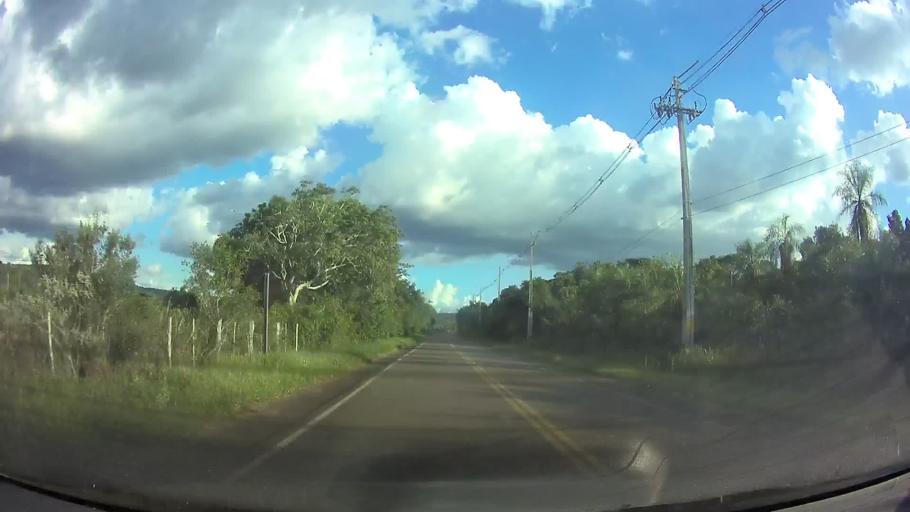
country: PY
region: Cordillera
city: Altos
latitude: -25.2361
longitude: -57.2307
